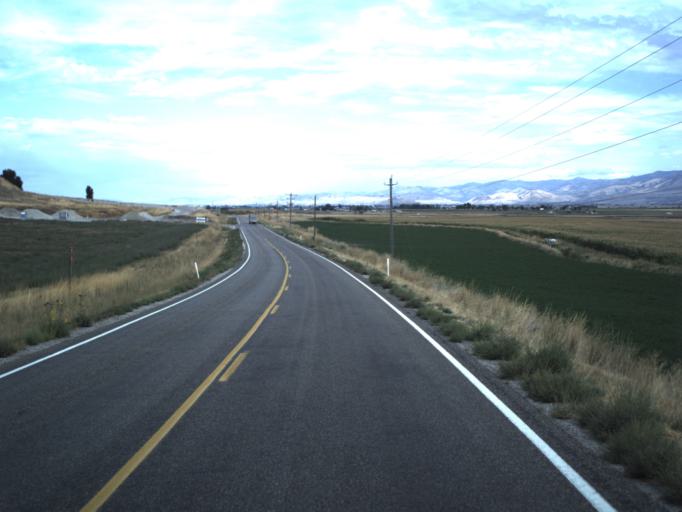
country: US
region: Utah
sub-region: Cache County
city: Benson
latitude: 41.8681
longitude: -111.9518
